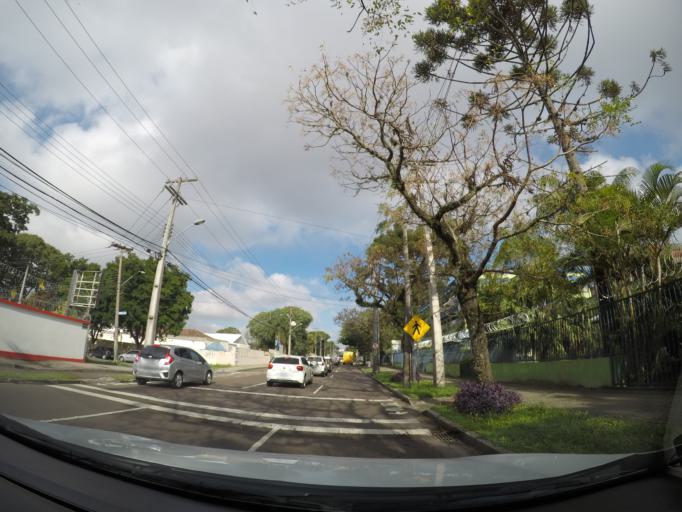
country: BR
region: Parana
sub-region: Curitiba
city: Curitiba
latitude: -25.4410
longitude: -49.2572
